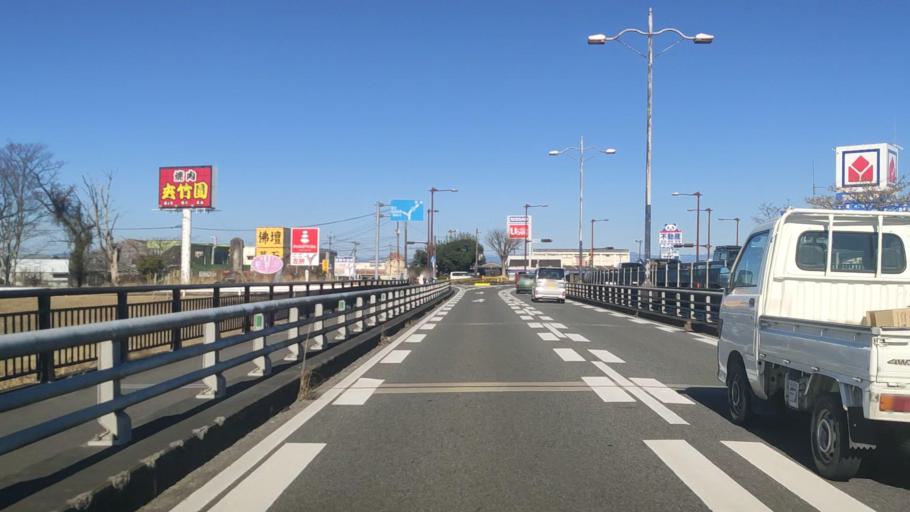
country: JP
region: Miyazaki
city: Miyakonojo
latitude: 31.7505
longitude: 131.0779
